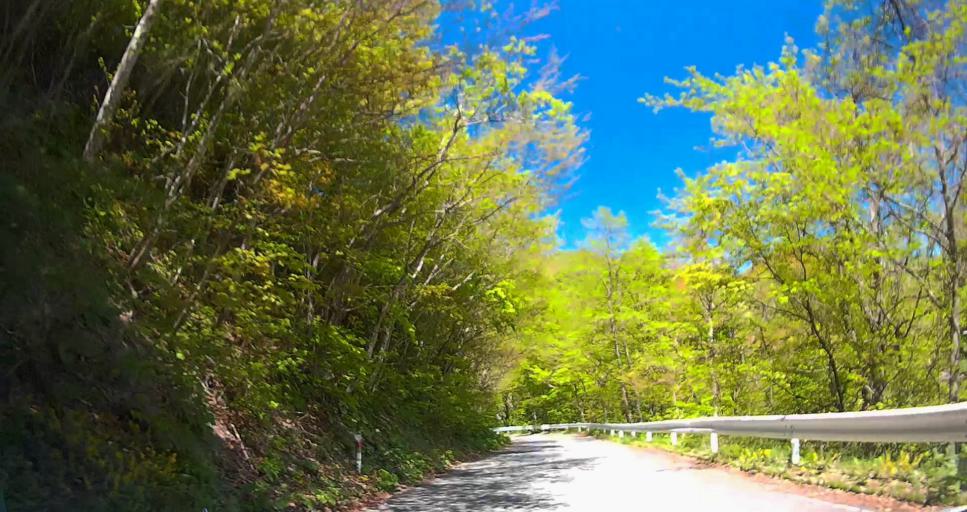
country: JP
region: Aomori
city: Mutsu
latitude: 41.3218
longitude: 140.8191
